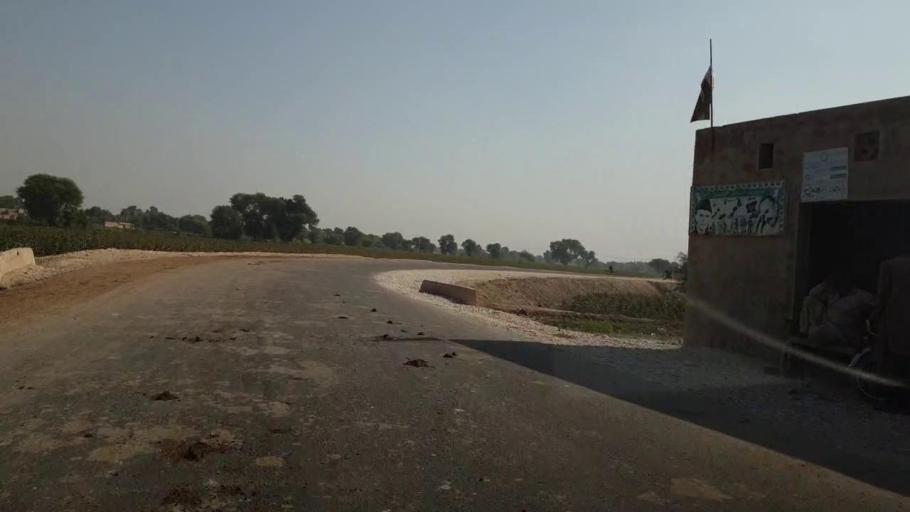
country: PK
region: Sindh
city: Dadu
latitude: 26.6751
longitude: 67.7764
